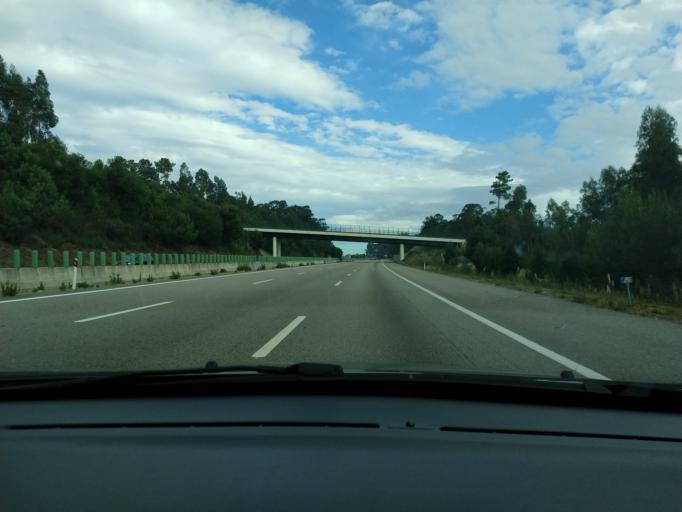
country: PT
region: Aveiro
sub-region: Santa Maria da Feira
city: Feira
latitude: 40.8969
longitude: -8.5680
